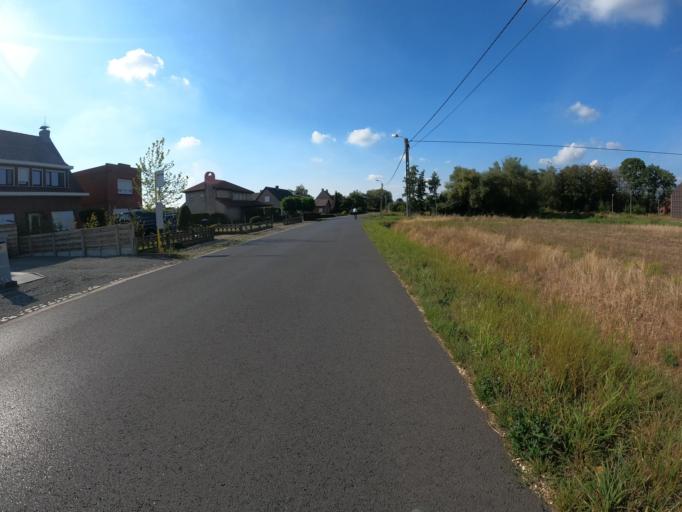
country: BE
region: Flanders
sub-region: Provincie Antwerpen
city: Berlaar
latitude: 51.0810
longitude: 4.6587
